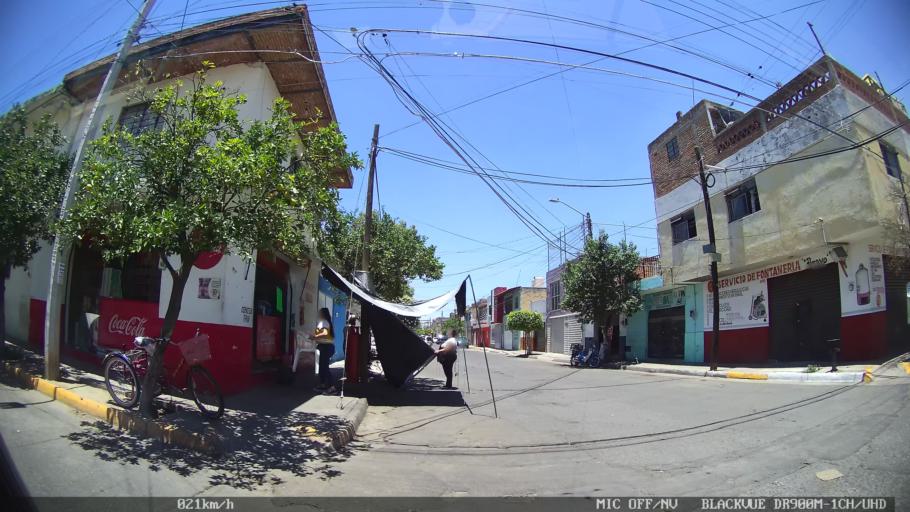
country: MX
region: Jalisco
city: Tlaquepaque
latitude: 20.6690
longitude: -103.2908
